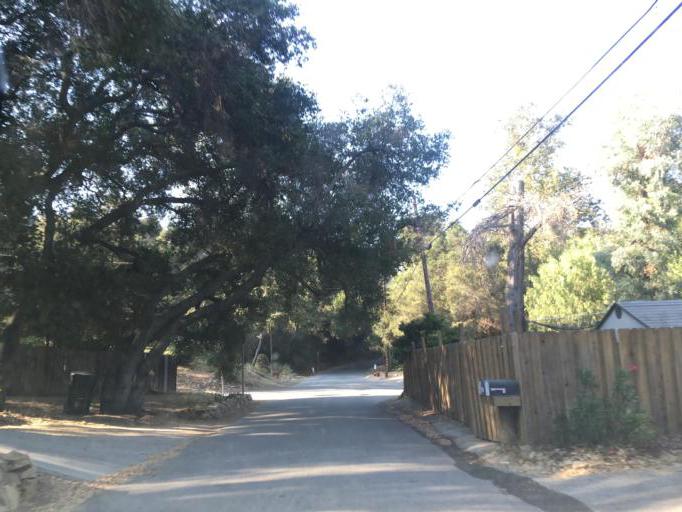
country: US
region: California
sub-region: Los Angeles County
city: Malibu Beach
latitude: 34.0832
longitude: -118.6868
